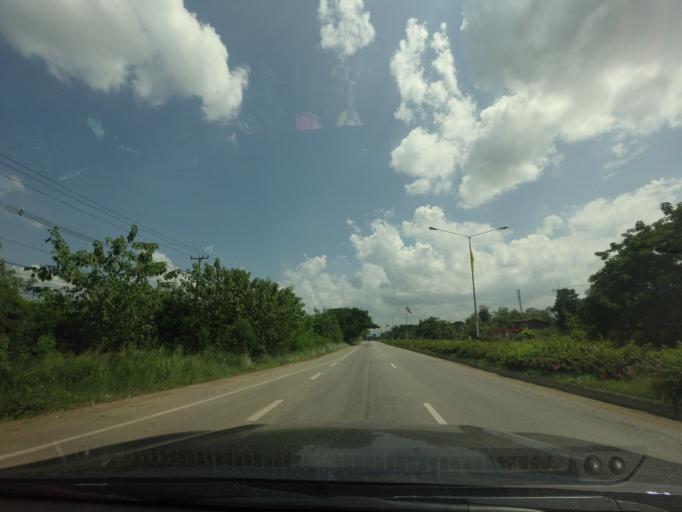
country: TH
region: Phetchabun
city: Phetchabun
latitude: 16.2537
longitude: 101.0633
